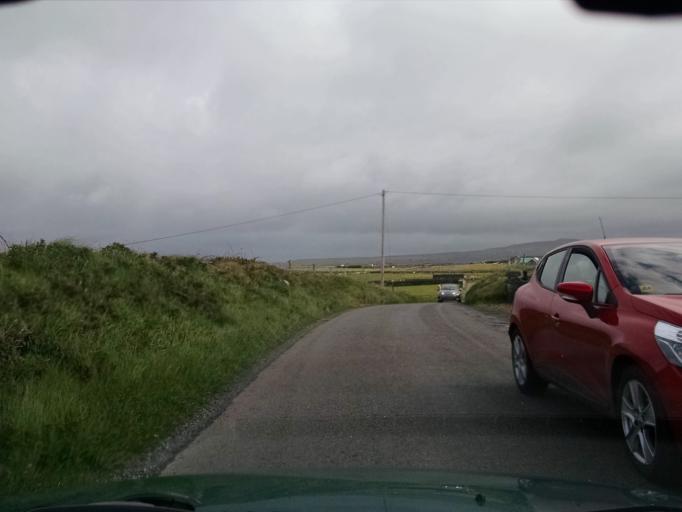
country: IE
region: Connaught
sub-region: County Galway
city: Bearna
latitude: 53.0319
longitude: -9.3652
